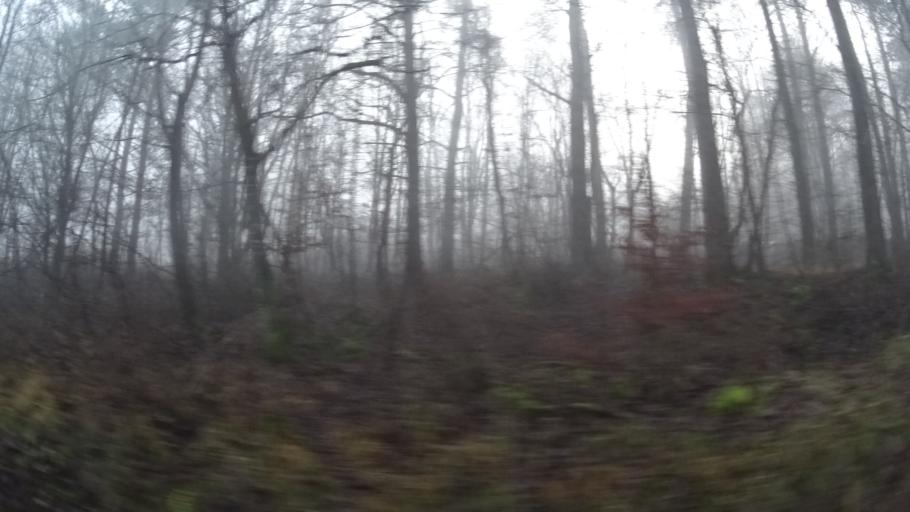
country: DE
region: Bavaria
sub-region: Regierungsbezirk Unterfranken
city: Kreuzwertheim
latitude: 49.7439
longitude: 9.5741
